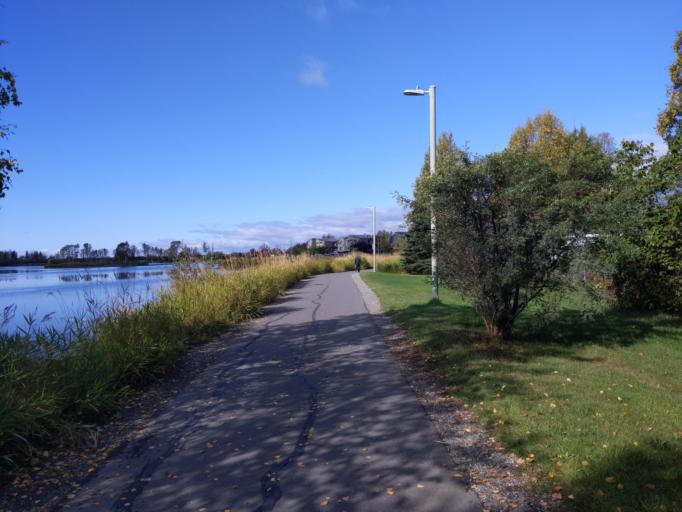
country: US
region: Alaska
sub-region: Anchorage Municipality
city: Anchorage
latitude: 61.2065
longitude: -149.9153
